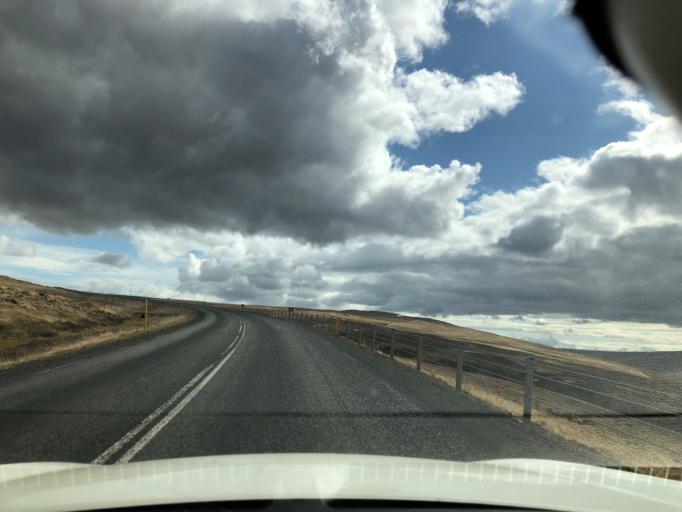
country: IS
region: Northwest
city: Saudarkrokur
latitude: 65.5121
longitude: -19.7626
